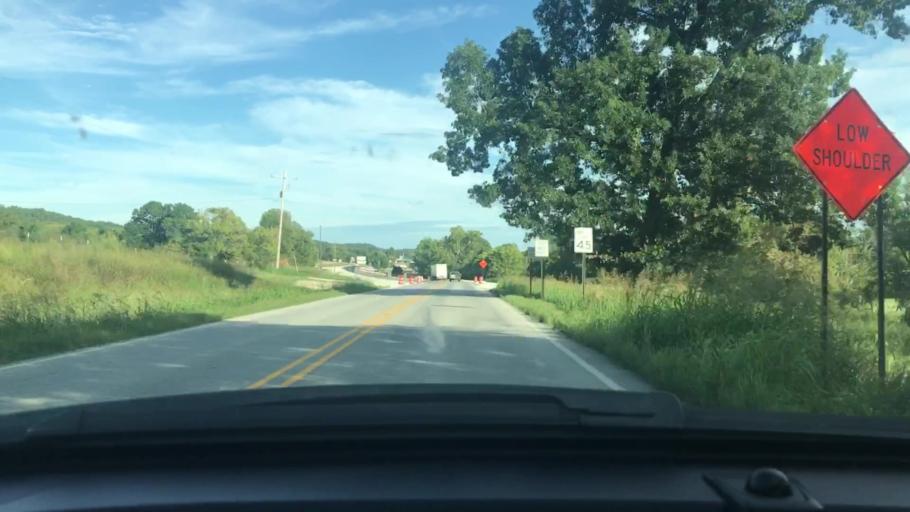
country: US
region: Arkansas
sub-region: Sharp County
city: Cherokee Village
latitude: 36.3054
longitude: -91.4514
